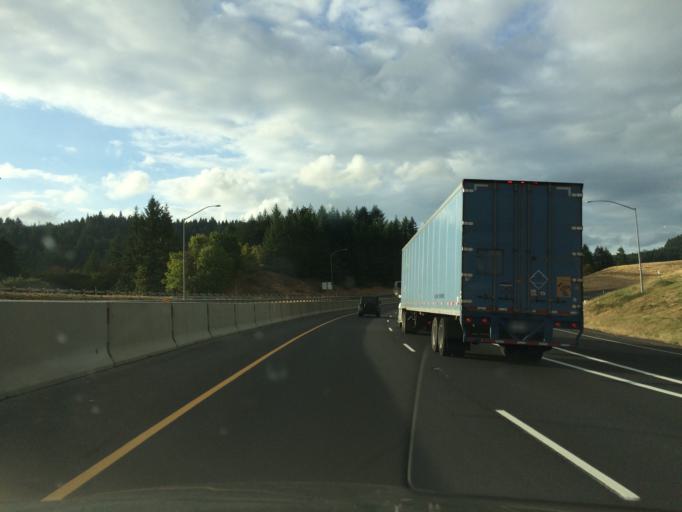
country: US
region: Oregon
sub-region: Douglas County
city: Drain
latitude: 43.7088
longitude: -123.2177
